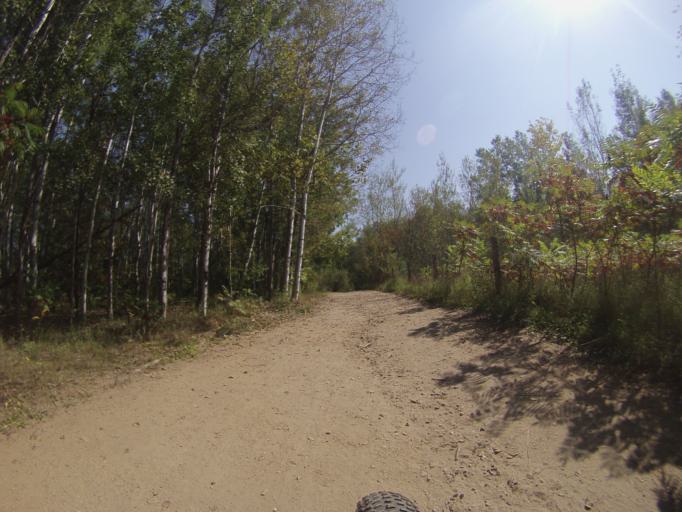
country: CA
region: Ontario
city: Ottawa
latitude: 45.3579
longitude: -75.6245
